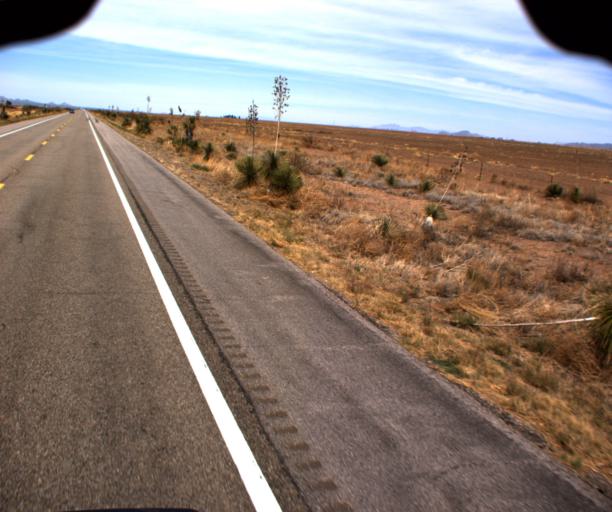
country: US
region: Arizona
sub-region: Cochise County
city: Pirtleville
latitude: 31.5435
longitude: -109.6584
